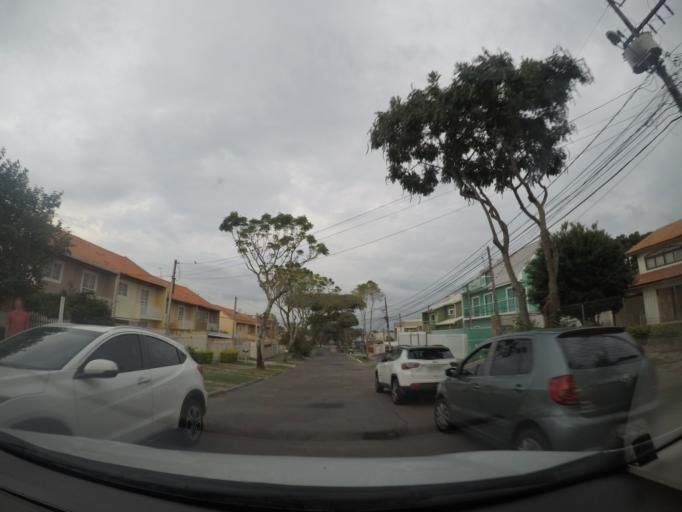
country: BR
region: Parana
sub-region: Sao Jose Dos Pinhais
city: Sao Jose dos Pinhais
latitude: -25.5150
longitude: -49.2378
